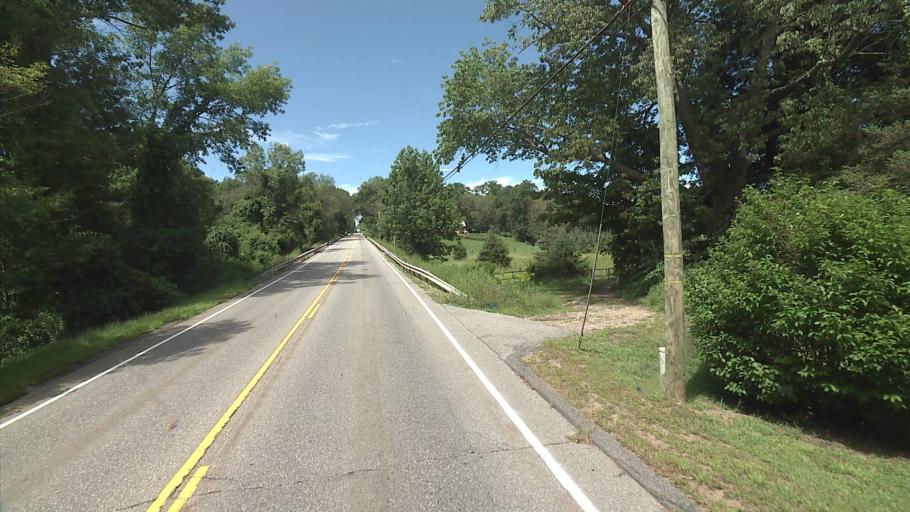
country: US
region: Connecticut
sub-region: Tolland County
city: Mansfield City
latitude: 41.7814
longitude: -72.2144
